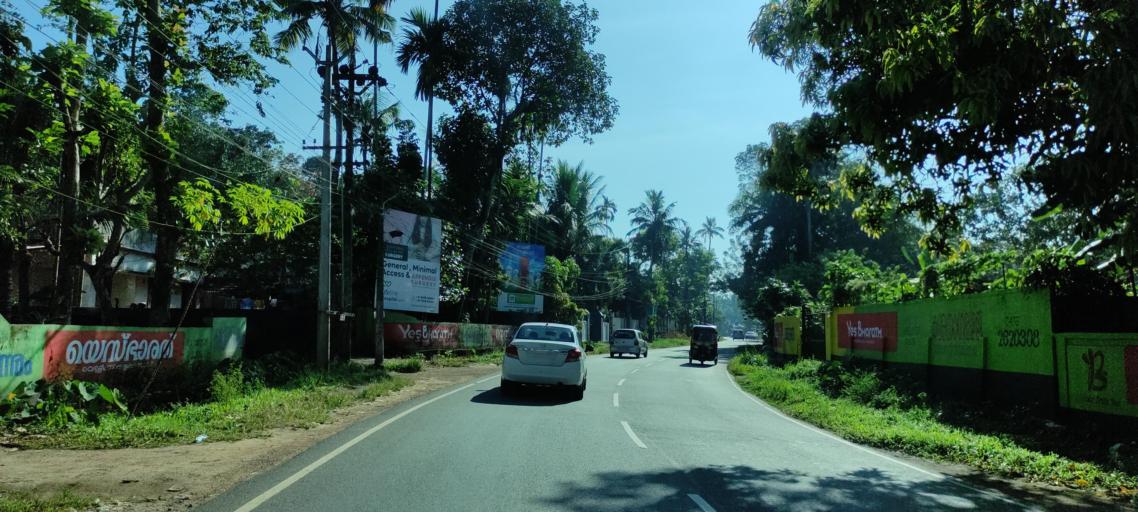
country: IN
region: Kerala
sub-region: Pattanamtitta
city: Adur
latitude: 9.1672
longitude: 76.6786
